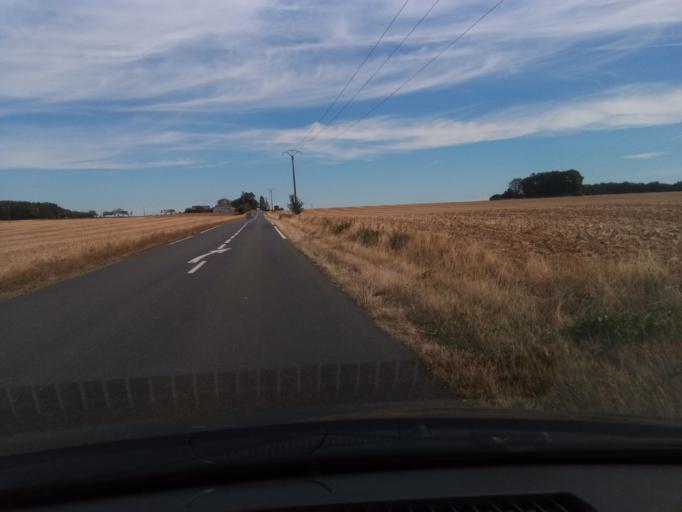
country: FR
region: Poitou-Charentes
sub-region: Departement de la Vienne
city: Chauvigny
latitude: 46.5399
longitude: 0.6924
